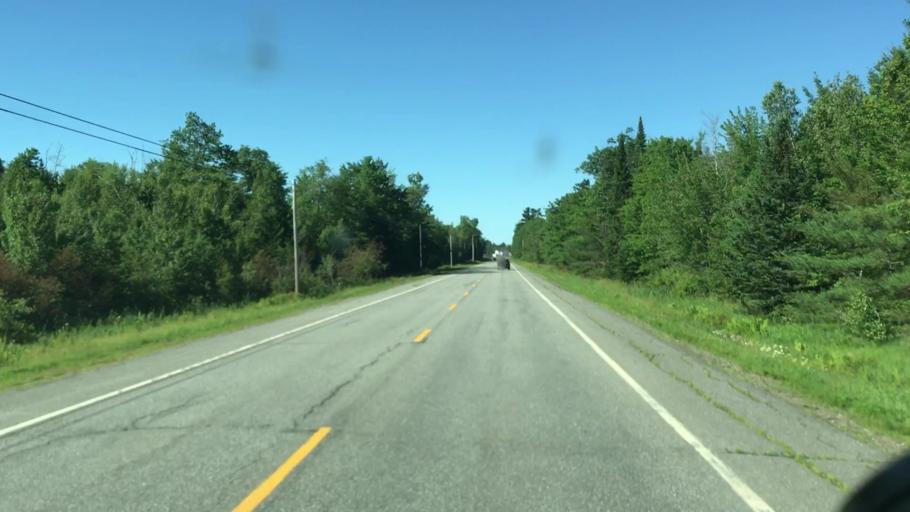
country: US
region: Maine
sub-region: Penobscot County
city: Enfield
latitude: 45.3048
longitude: -68.6132
